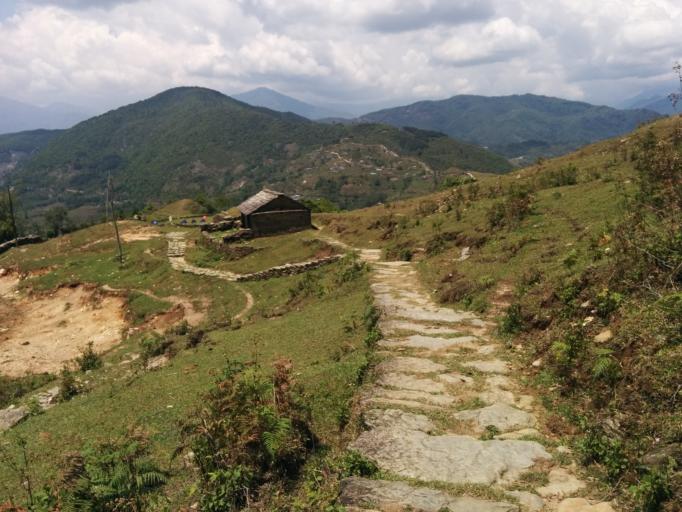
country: NP
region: Western Region
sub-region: Gandaki Zone
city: Pokhara
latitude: 28.2582
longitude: 83.8217
